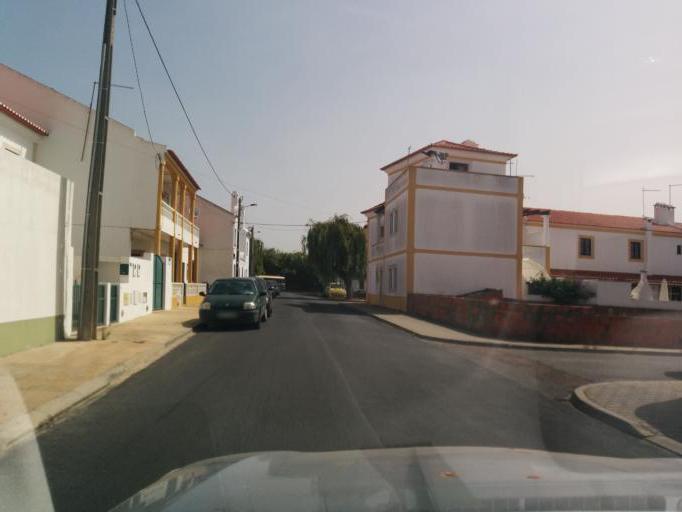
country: PT
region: Beja
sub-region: Odemira
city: Vila Nova de Milfontes
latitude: 37.7298
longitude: -8.7782
